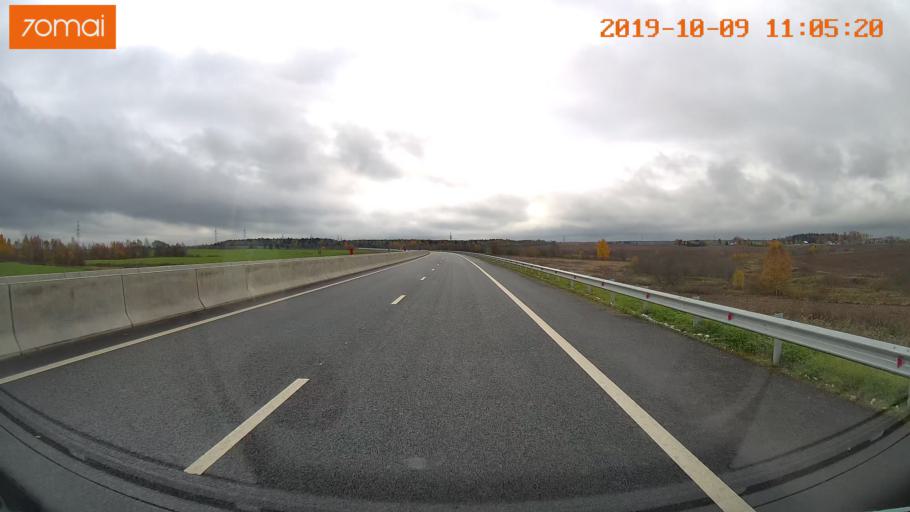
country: RU
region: Vologda
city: Molochnoye
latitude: 59.2015
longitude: 39.7592
